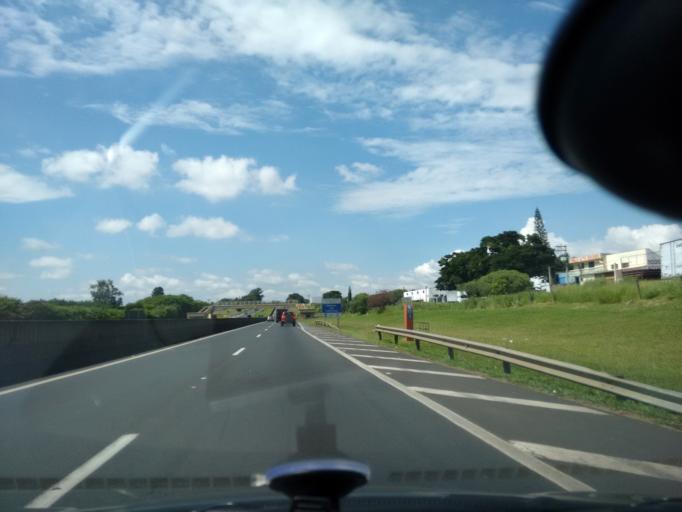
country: BR
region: Sao Paulo
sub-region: Sao Carlos
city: Sao Carlos
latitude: -21.9944
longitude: -47.8789
